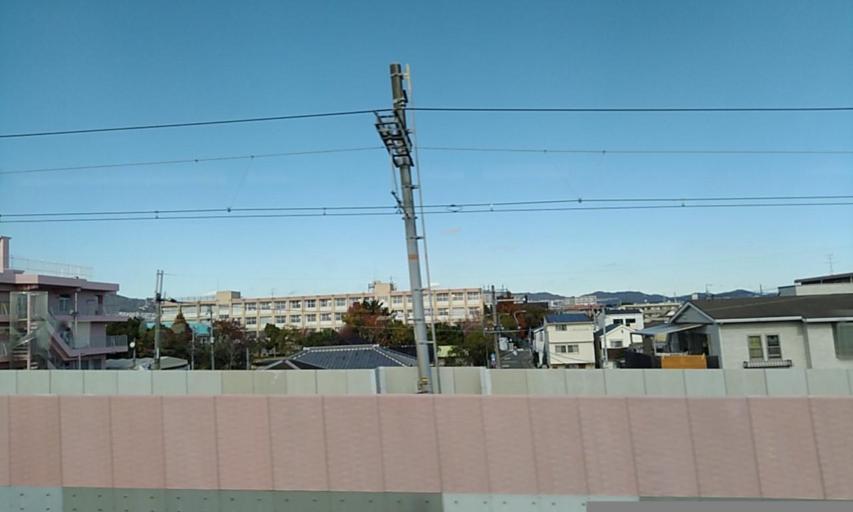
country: JP
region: Hyogo
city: Itami
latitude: 34.7494
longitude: 135.3788
